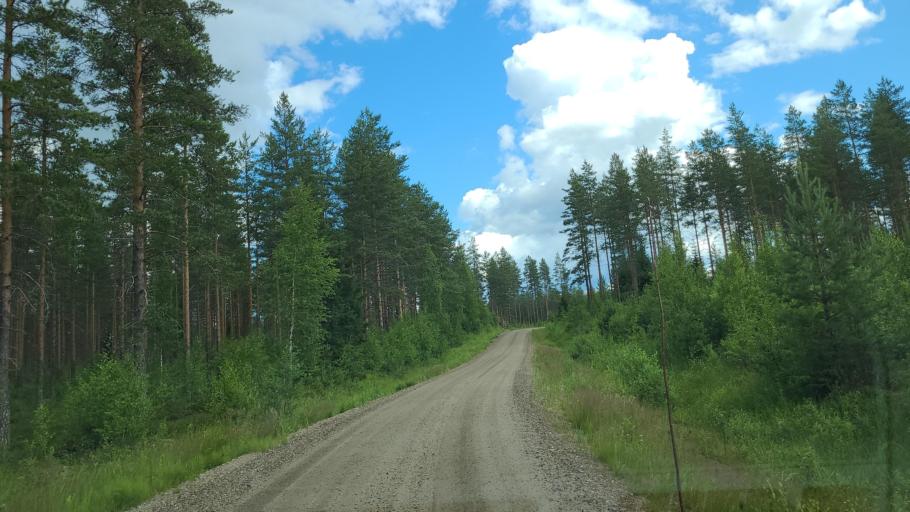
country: FI
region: Northern Savo
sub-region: Koillis-Savo
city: Kaavi
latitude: 63.0338
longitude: 28.7842
